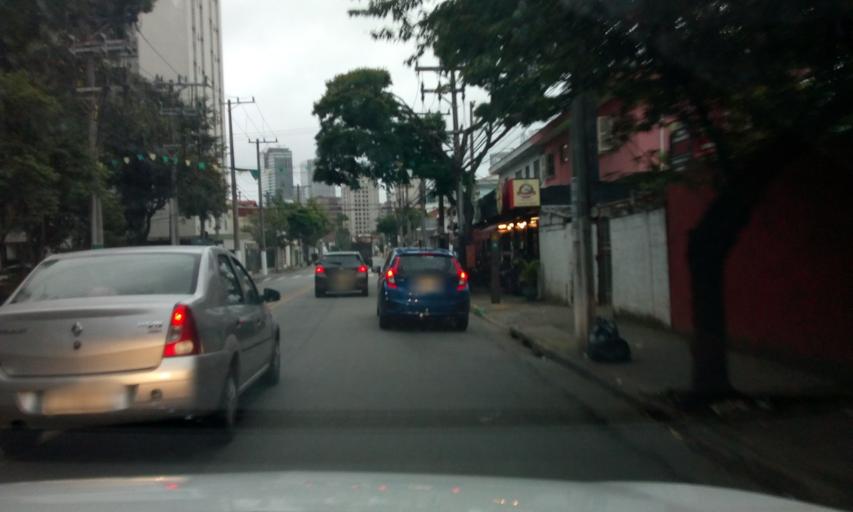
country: BR
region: Sao Paulo
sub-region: Sao Paulo
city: Sao Paulo
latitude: -23.6009
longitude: -46.6890
